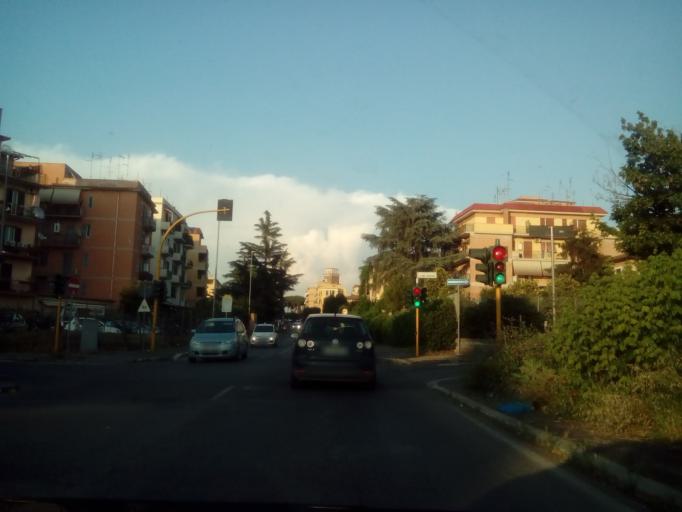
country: IT
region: Latium
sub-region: Citta metropolitana di Roma Capitale
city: Rome
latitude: 41.9034
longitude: 12.5852
